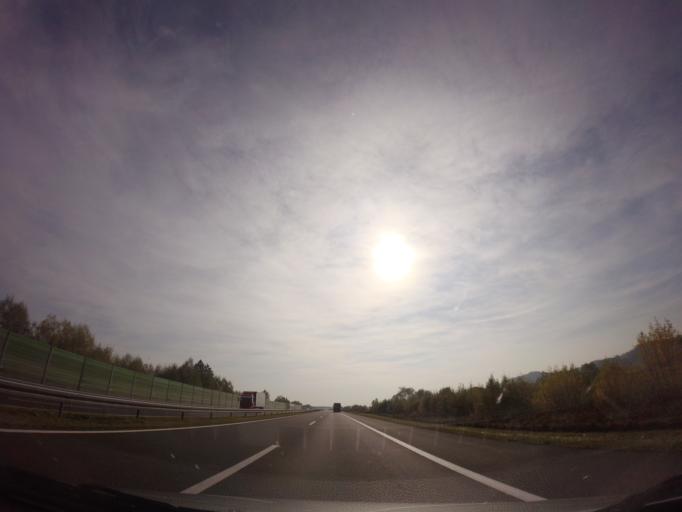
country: HR
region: Varazdinska
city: Remetinec
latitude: 46.0509
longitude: 16.2964
